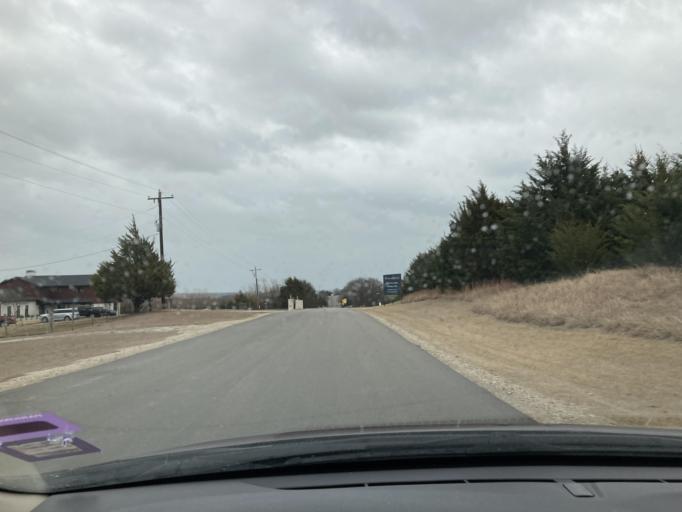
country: US
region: Texas
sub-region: Collin County
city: Lucas
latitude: 33.0805
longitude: -96.5570
